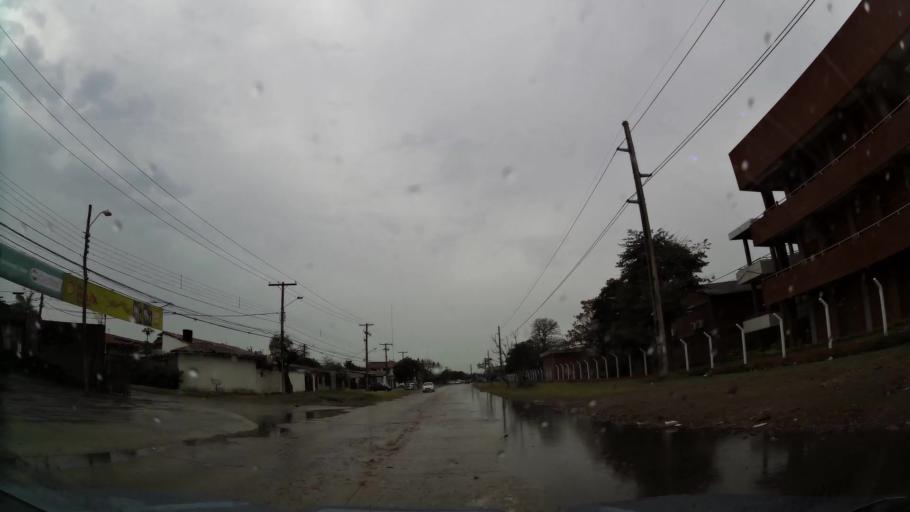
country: BO
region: Santa Cruz
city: Santa Cruz de la Sierra
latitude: -17.7783
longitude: -63.1532
